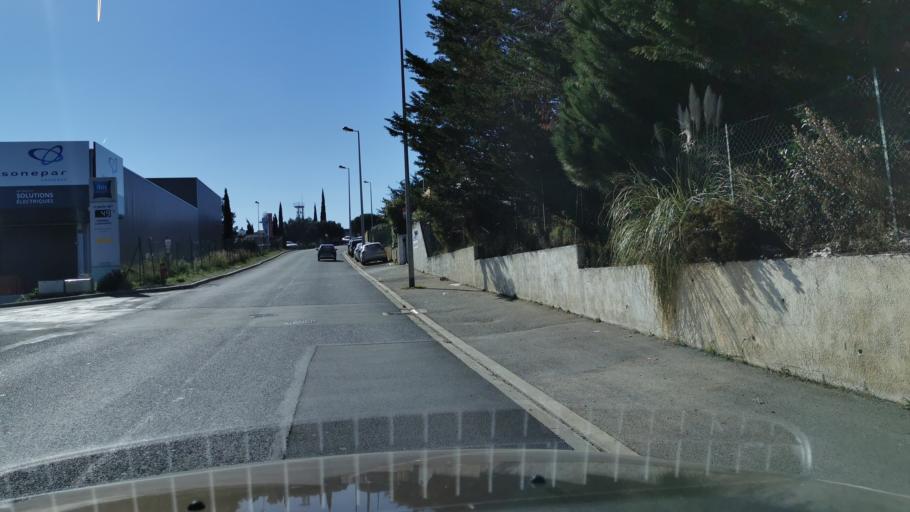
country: FR
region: Languedoc-Roussillon
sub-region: Departement de l'Aude
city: Narbonne
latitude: 43.1541
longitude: 2.9786
